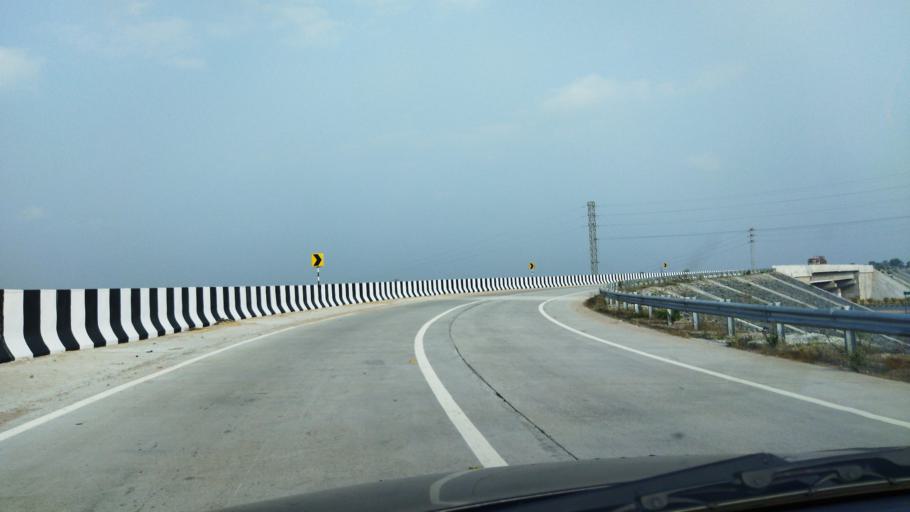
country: IN
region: Telangana
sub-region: Nalgonda
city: Nalgonda
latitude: 17.1670
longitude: 79.3953
